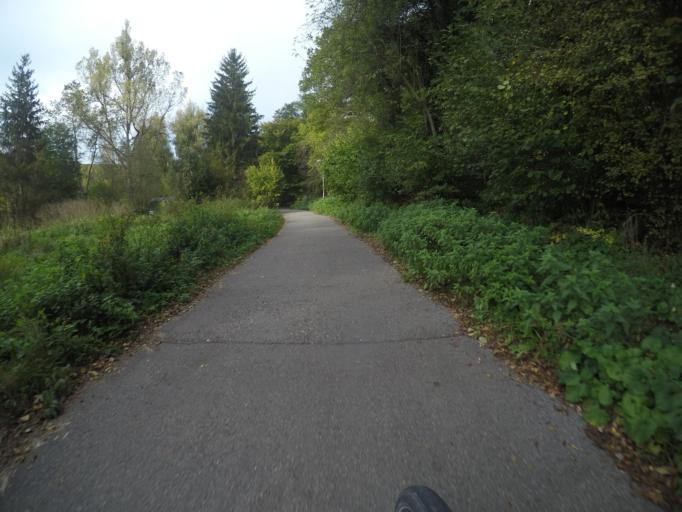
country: DE
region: Baden-Wuerttemberg
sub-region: Tuebingen Region
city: Tuebingen
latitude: 48.5370
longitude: 9.0787
